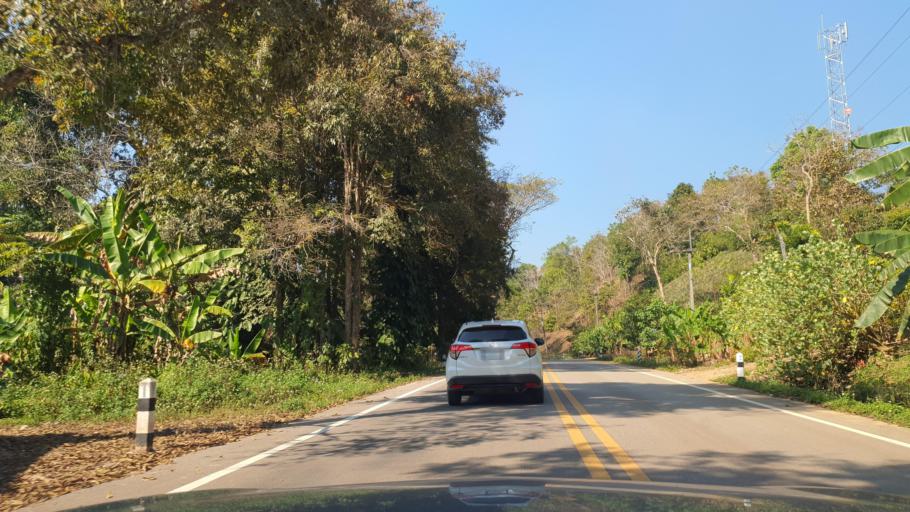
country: TH
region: Chiang Rai
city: Mae Lao
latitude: 19.8626
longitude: 99.6517
